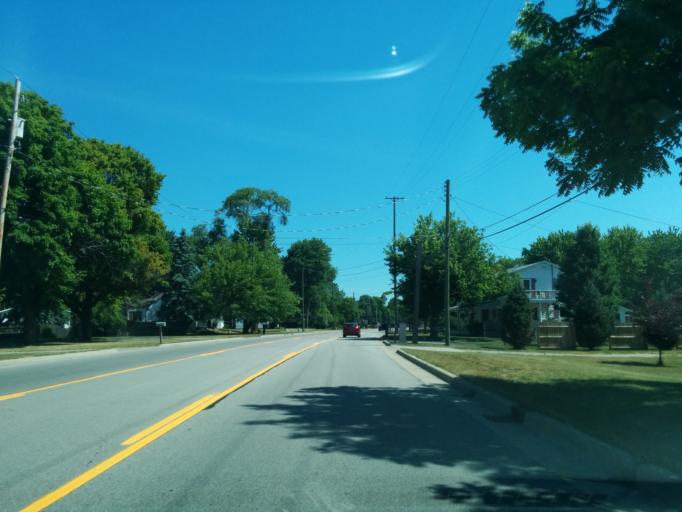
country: US
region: Michigan
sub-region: Bay County
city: Bay City
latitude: 43.5779
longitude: -83.9230
